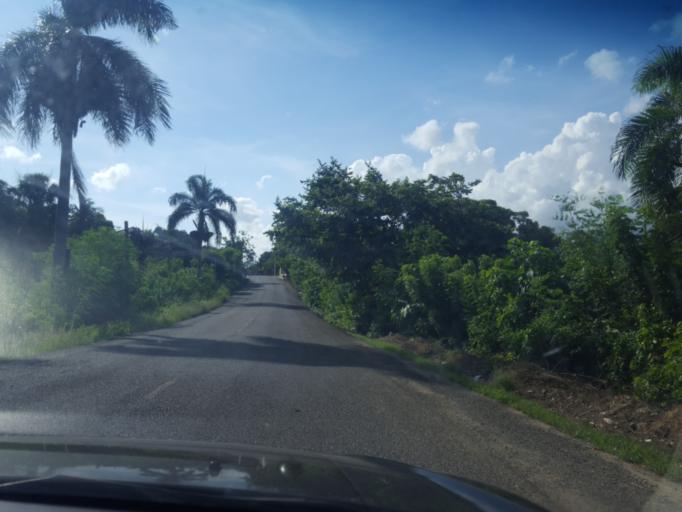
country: DO
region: Santiago
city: Licey al Medio
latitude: 19.3773
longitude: -70.6110
